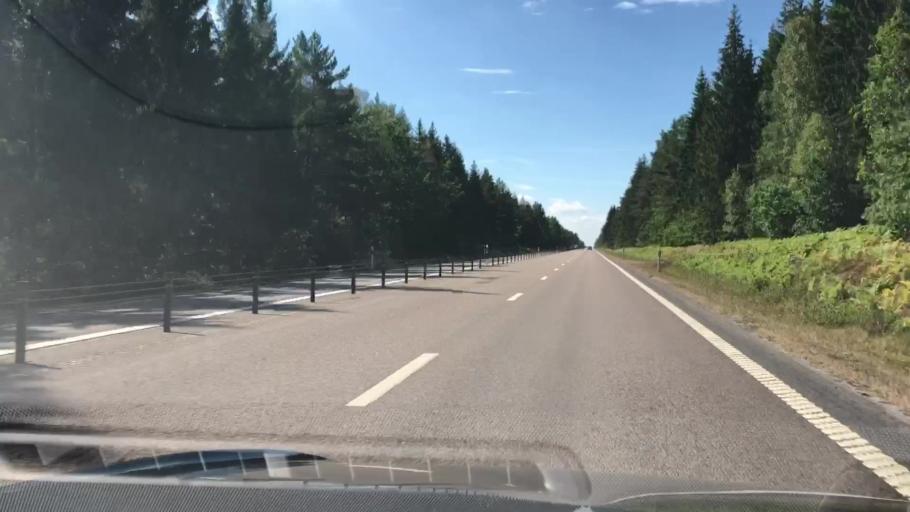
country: SE
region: Kalmar
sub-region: Monsteras Kommun
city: Moensteras
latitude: 57.0157
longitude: 16.4262
